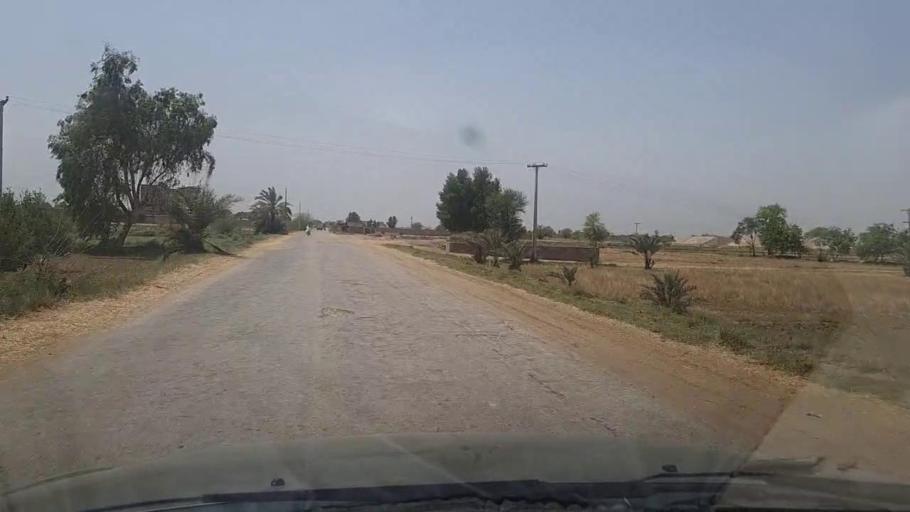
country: PK
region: Sindh
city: Karaundi
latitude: 26.8812
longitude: 68.3052
